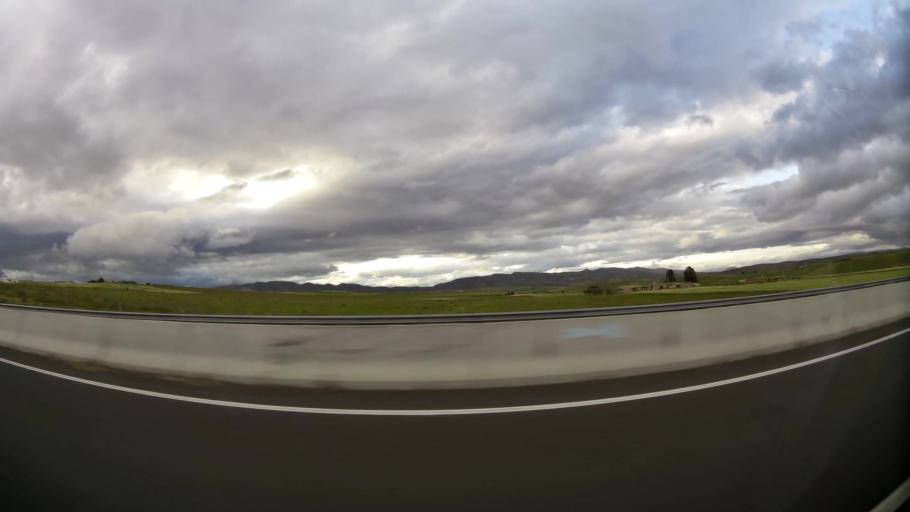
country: MA
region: Taza-Al Hoceima-Taounate
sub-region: Taza
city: Taza
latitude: 34.2535
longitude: -3.8874
